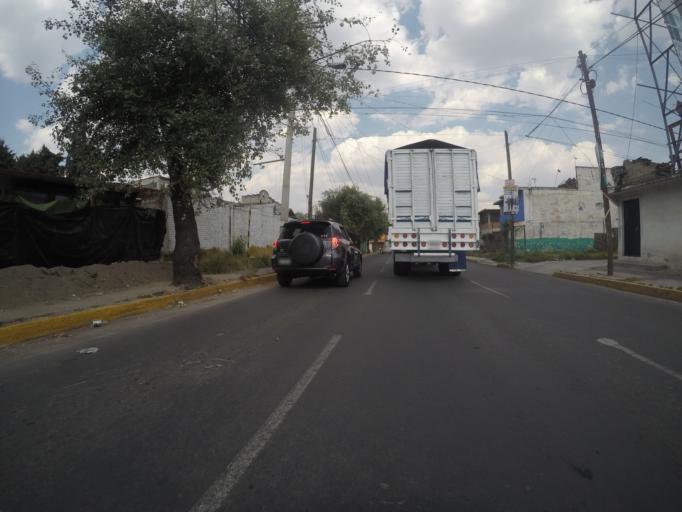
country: MX
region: Mexico
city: San Buenaventura
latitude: 19.2564
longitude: -99.6606
